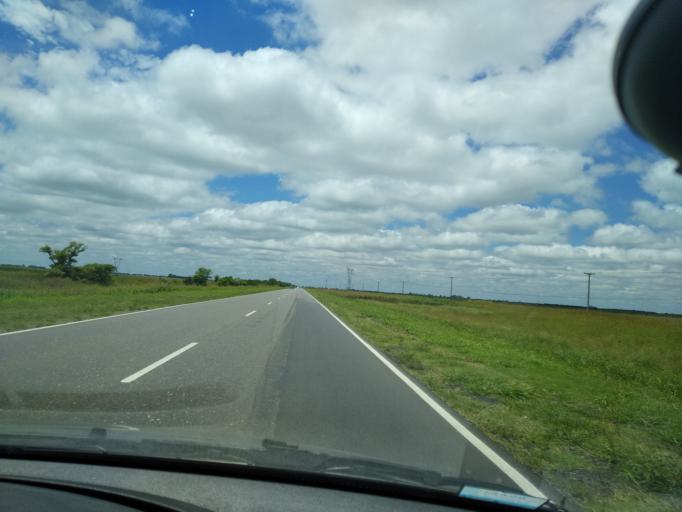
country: AR
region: Cordoba
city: Toledo
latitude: -31.6463
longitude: -64.0456
